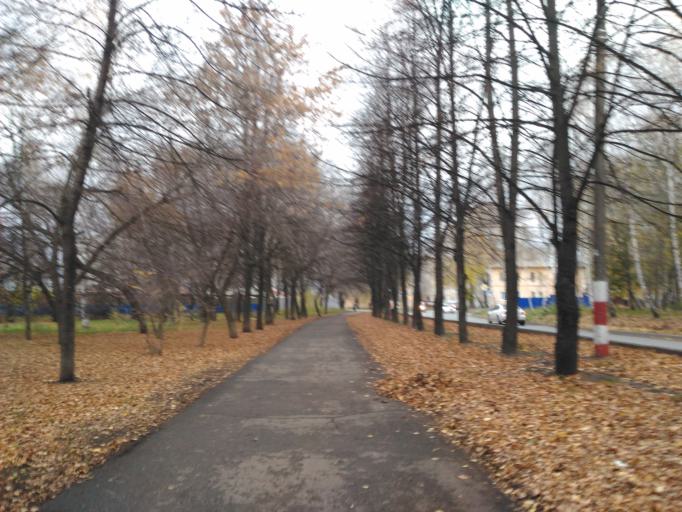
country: RU
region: Ulyanovsk
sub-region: Ulyanovskiy Rayon
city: Ulyanovsk
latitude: 54.3400
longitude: 48.3930
